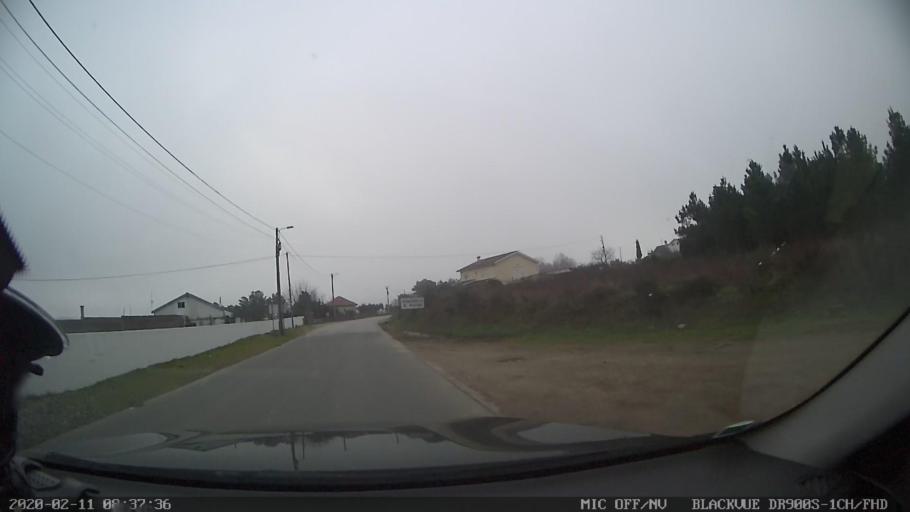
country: PT
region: Vila Real
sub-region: Sabrosa
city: Sabrosa
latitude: 41.2564
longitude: -7.5875
